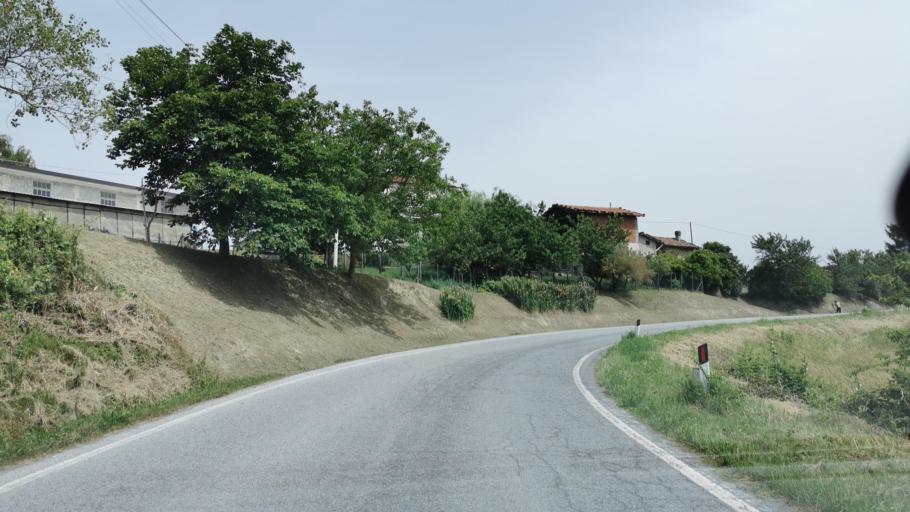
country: IT
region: Piedmont
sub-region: Provincia di Cuneo
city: Sale San Giovanni
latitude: 44.4158
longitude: 8.0851
